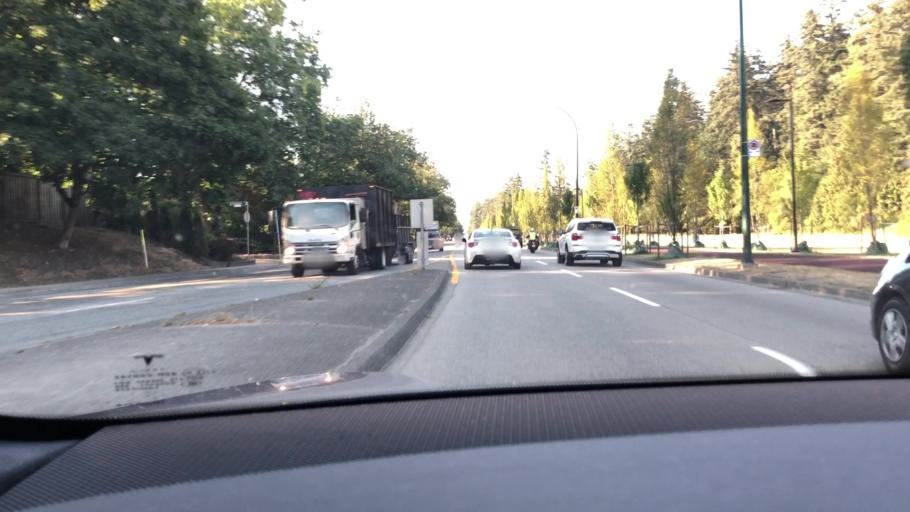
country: CA
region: British Columbia
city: Burnaby
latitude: 49.2228
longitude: -123.0235
